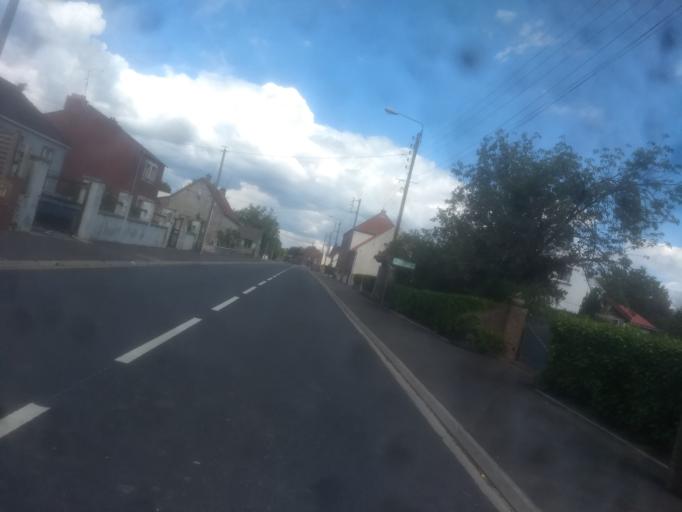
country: FR
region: Nord-Pas-de-Calais
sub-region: Departement du Pas-de-Calais
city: Croisilles
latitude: 50.2246
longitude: 2.8336
